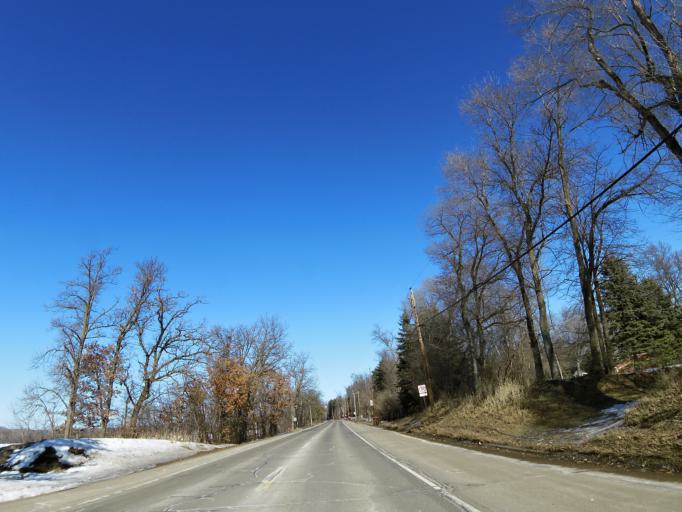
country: US
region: Minnesota
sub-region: Washington County
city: Lake Elmo
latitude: 44.9836
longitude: -92.8810
